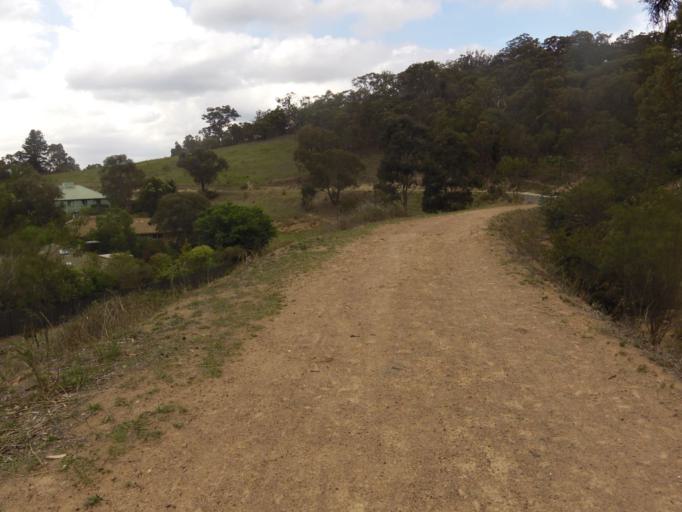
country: AU
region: Australian Capital Territory
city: Forrest
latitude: -35.3613
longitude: 149.1130
